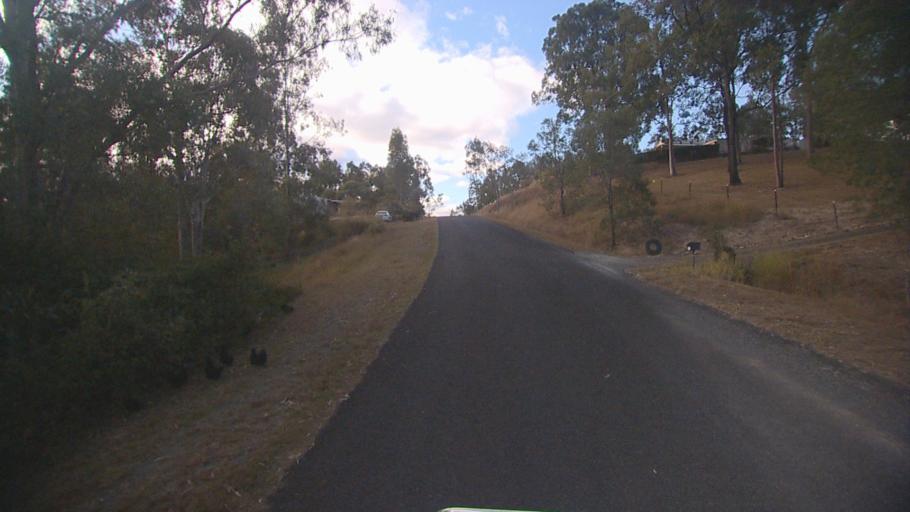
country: AU
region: Queensland
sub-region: Logan
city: Cedar Vale
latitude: -27.9049
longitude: 153.0727
